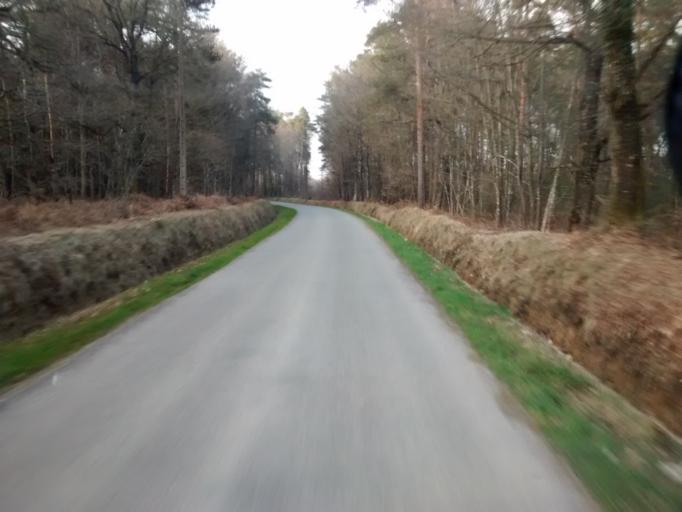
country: FR
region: Brittany
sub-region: Departement des Cotes-d'Armor
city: Merdrignac
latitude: 48.1256
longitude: -2.3881
